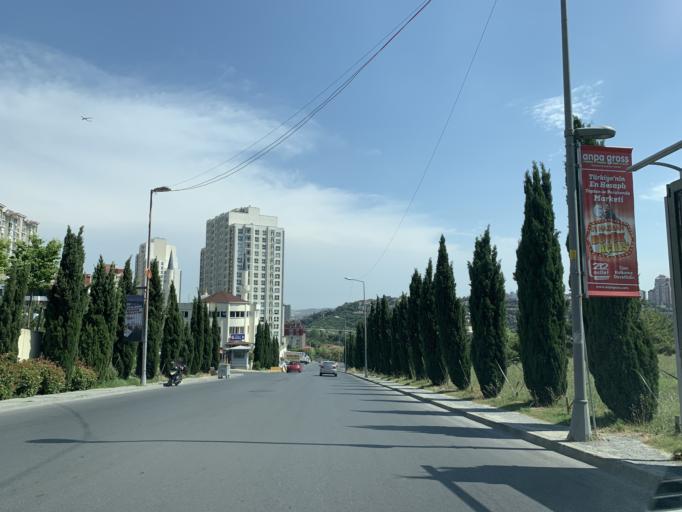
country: TR
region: Istanbul
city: Esenyurt
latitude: 41.0761
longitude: 28.6912
